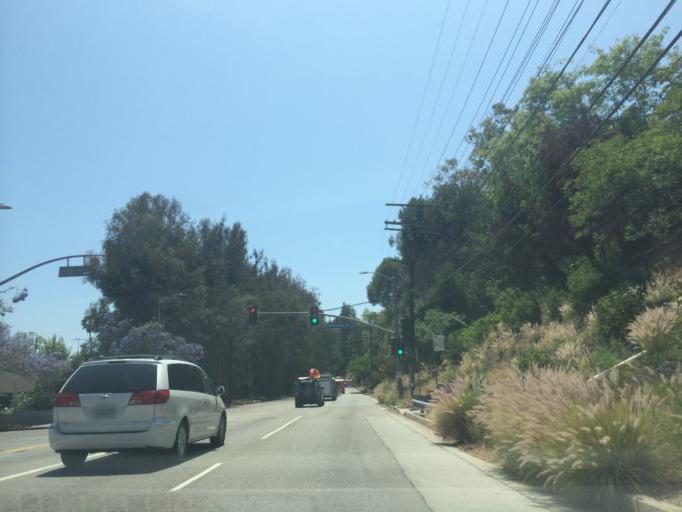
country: US
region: California
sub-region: Los Angeles County
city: Santa Monica
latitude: 34.0558
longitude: -118.4969
